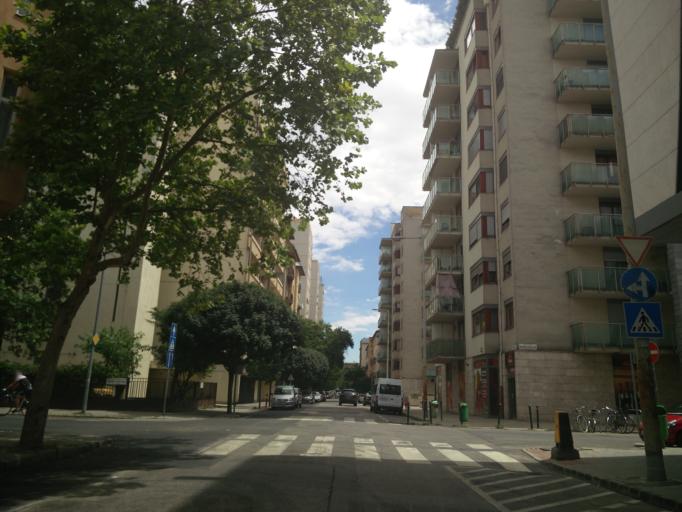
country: HU
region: Budapest
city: Budapest VI. keruelet
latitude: 47.5237
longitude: 19.0589
